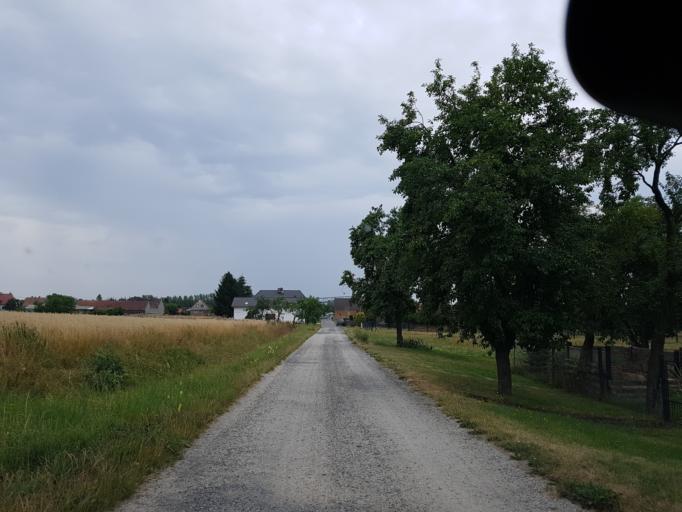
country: DE
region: Brandenburg
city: Sallgast
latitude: 51.5981
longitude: 13.7817
